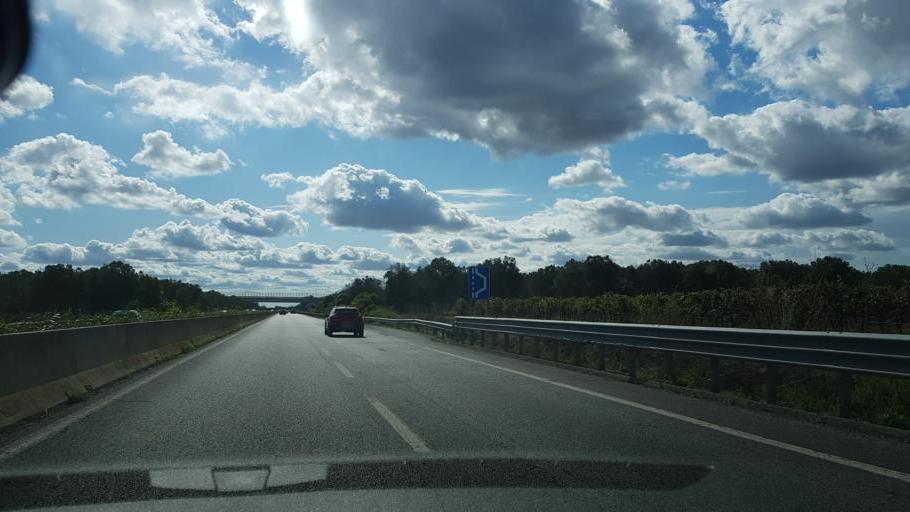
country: IT
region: Apulia
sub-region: Provincia di Brindisi
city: San Pietro Vernotico
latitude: 40.5387
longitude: 18.0042
